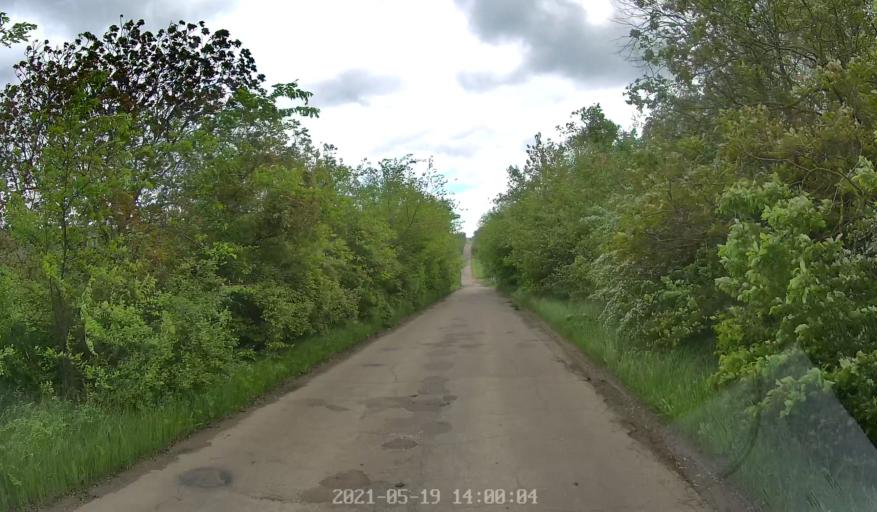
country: MD
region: Chisinau
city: Chisinau
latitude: 47.0368
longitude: 28.9292
